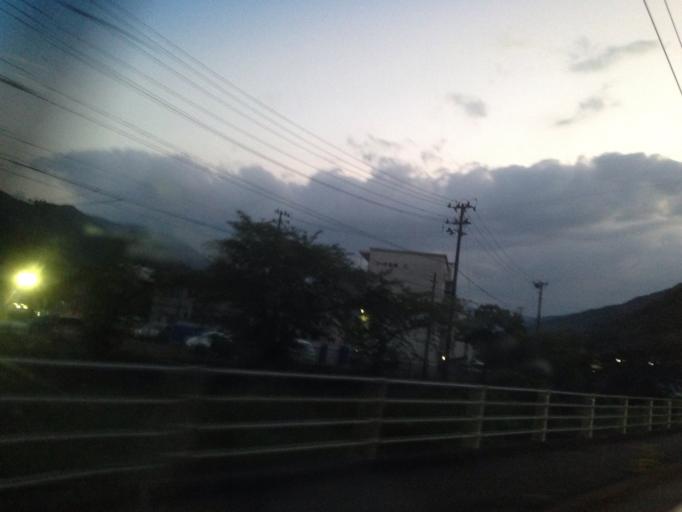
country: JP
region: Iwate
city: Kamaishi
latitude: 39.2563
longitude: 141.8172
